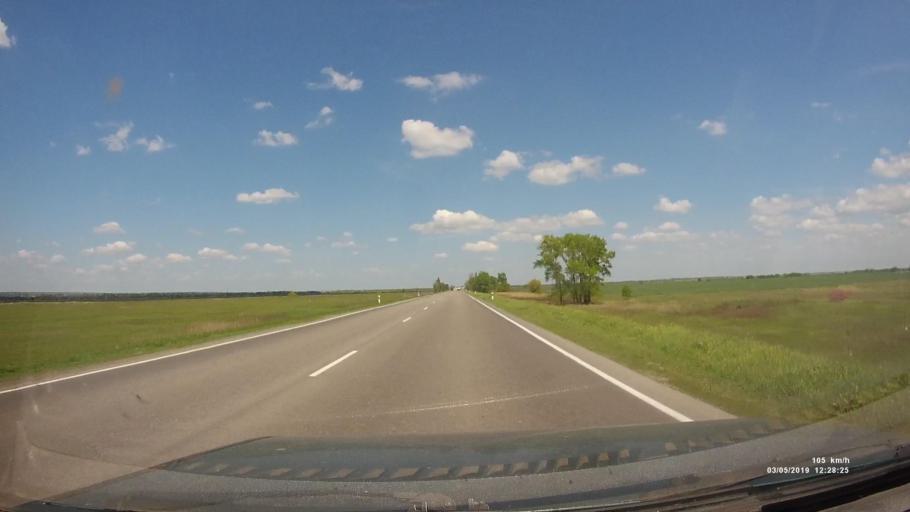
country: RU
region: Rostov
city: Semikarakorsk
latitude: 47.4732
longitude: 40.7280
